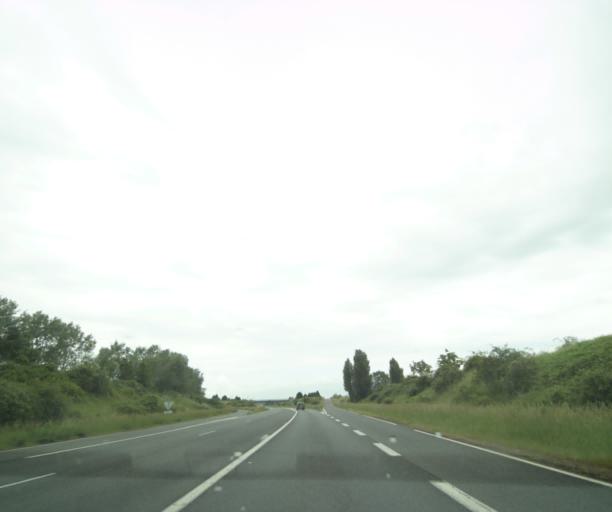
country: FR
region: Poitou-Charentes
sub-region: Departement des Deux-Sevres
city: Airvault
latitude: 46.8239
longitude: -0.2041
